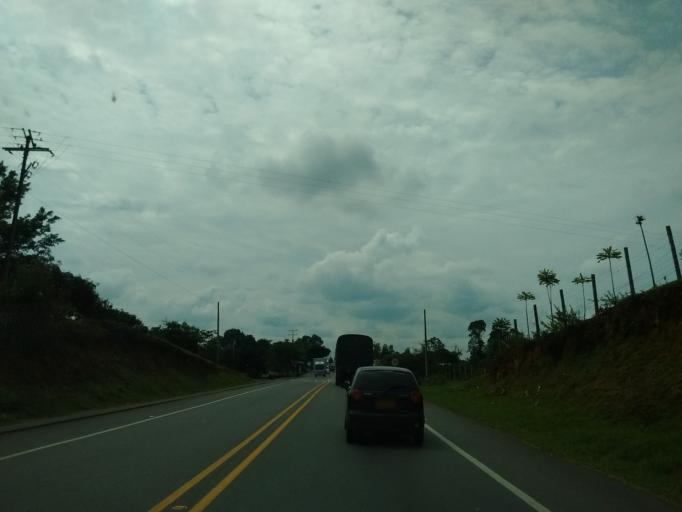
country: CO
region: Cauca
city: Morales
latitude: 2.7591
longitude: -76.5541
